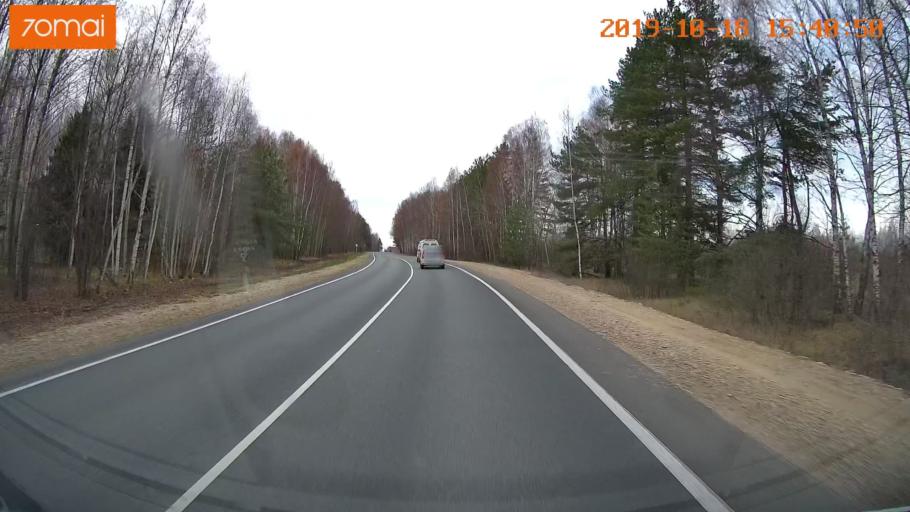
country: RU
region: Vladimir
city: Golovino
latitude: 55.9393
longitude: 40.5909
